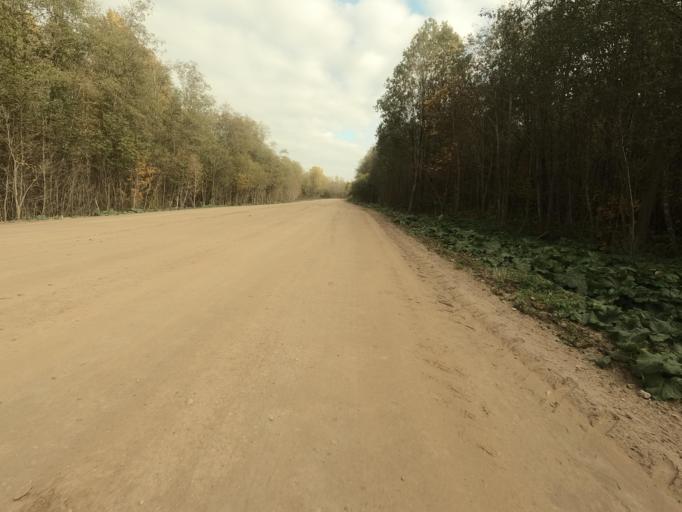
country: RU
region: Novgorod
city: Batetskiy
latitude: 58.8005
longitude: 30.6418
